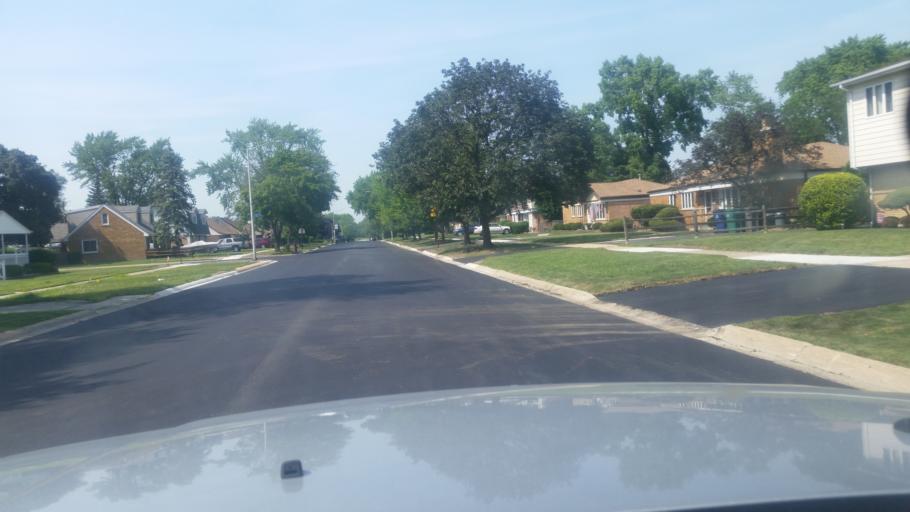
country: US
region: Illinois
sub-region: Cook County
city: Chicago Ridge
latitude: 41.6953
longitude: -87.7693
